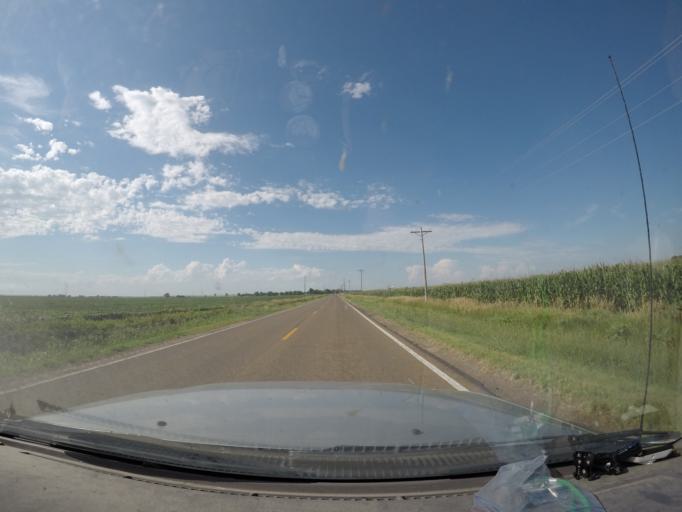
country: US
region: Nebraska
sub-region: Buffalo County
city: Kearney
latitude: 40.6896
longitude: -99.2557
